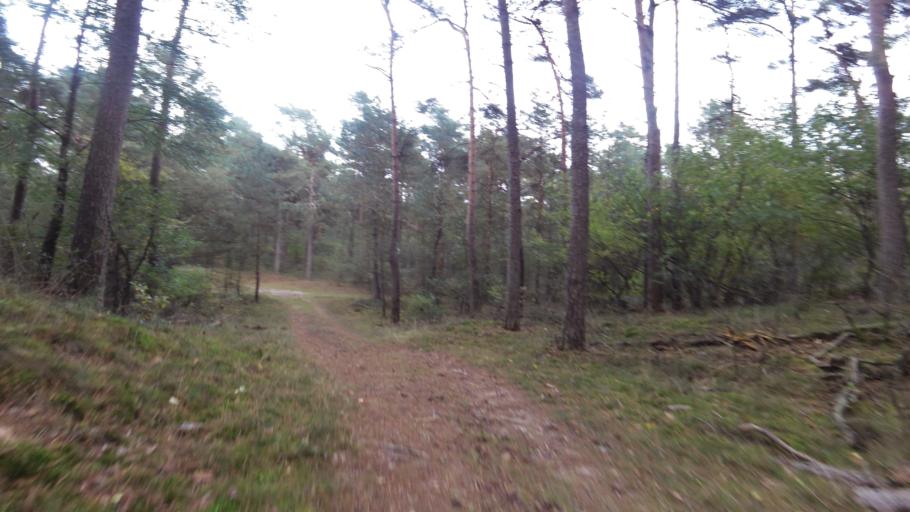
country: NL
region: Gelderland
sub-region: Gemeente Ede
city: Harskamp
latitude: 52.1570
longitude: 5.7515
